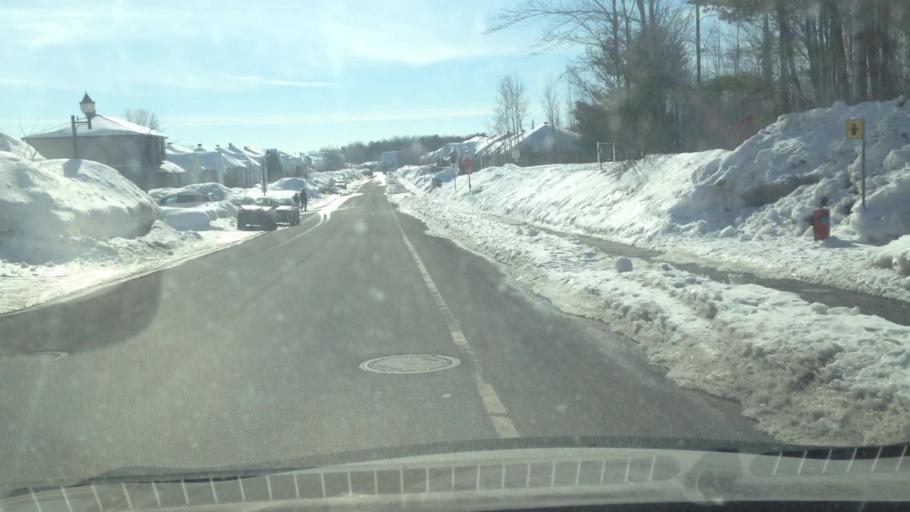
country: CA
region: Quebec
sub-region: Laurentides
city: Saint-Jerome
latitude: 45.7774
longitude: -73.9714
